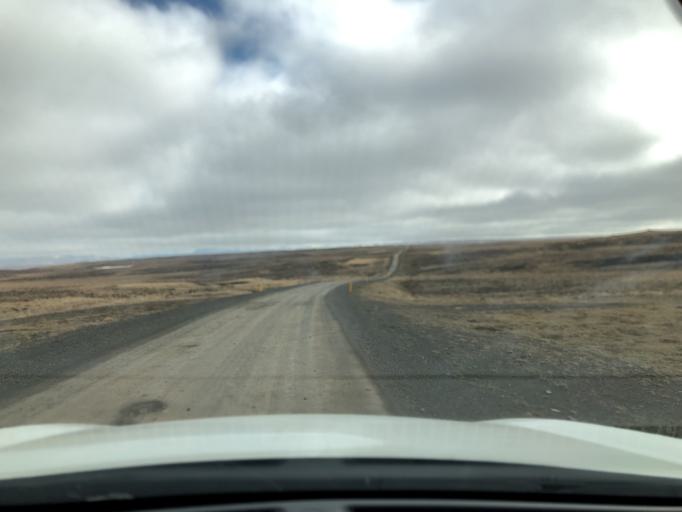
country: IS
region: West
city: Borgarnes
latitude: 65.2233
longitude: -21.2397
